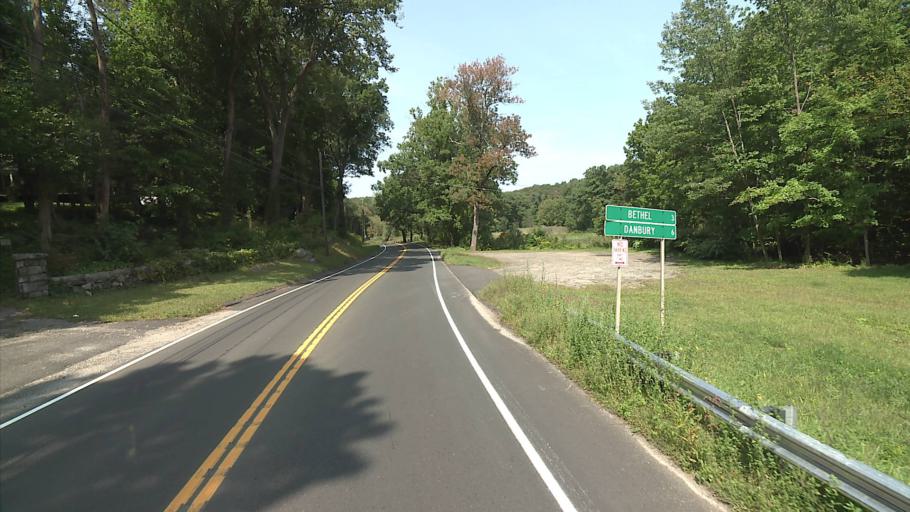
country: US
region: Connecticut
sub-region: Fairfield County
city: Bethel
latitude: 41.3398
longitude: -73.3815
